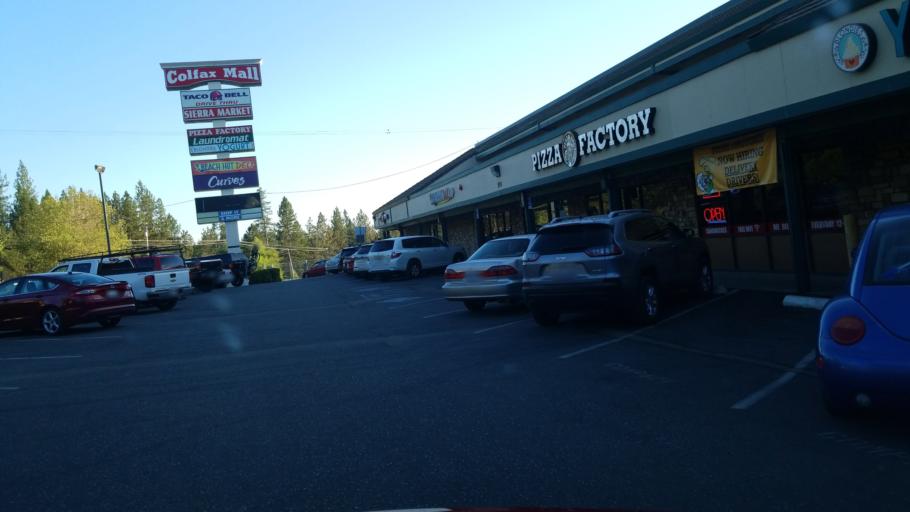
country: US
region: California
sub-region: Placer County
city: Colfax
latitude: 39.0939
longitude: -120.9510
